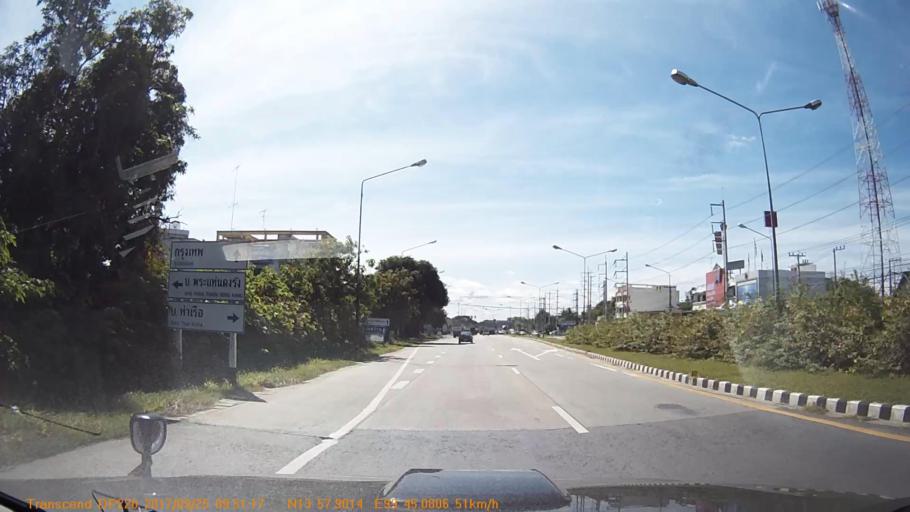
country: TH
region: Kanchanaburi
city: Tha Maka
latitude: 13.9649
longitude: 99.7515
